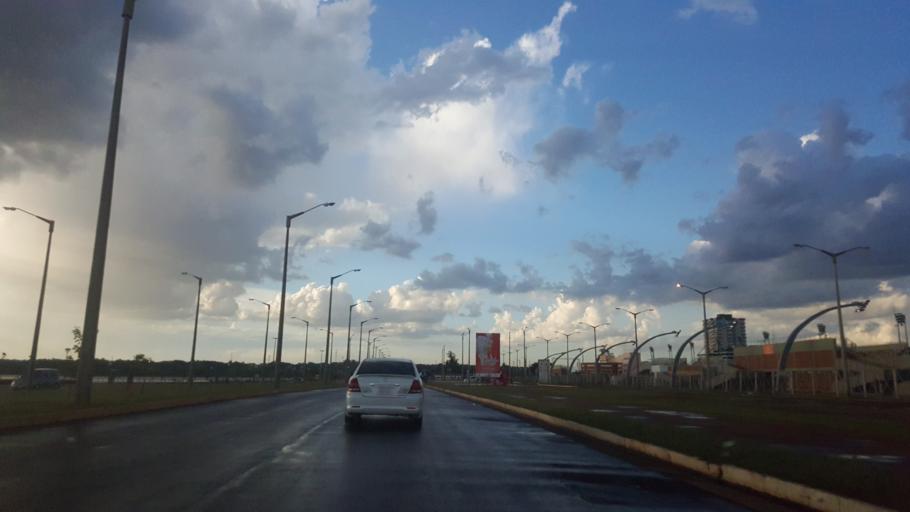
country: PY
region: Itapua
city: Encarnacion
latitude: -27.3307
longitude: -55.8751
